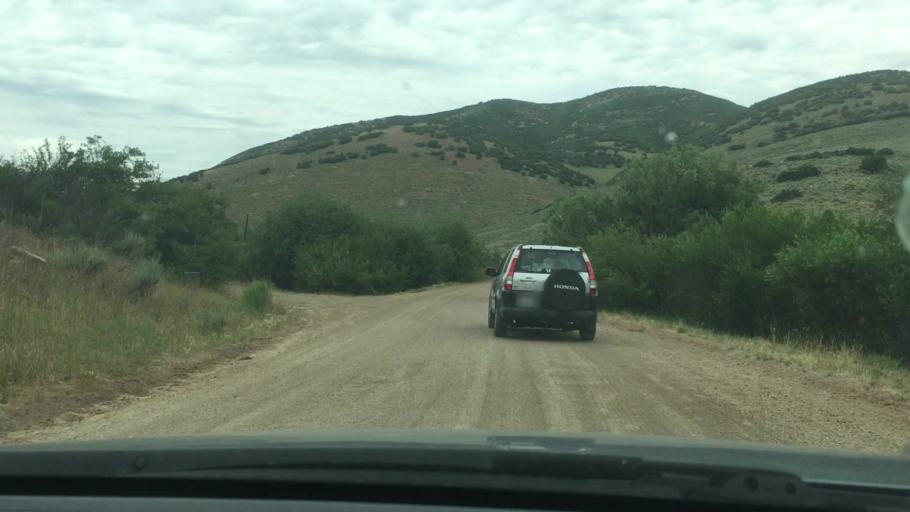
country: US
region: Utah
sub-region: Summit County
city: Summit Park
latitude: 40.7752
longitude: -111.5887
